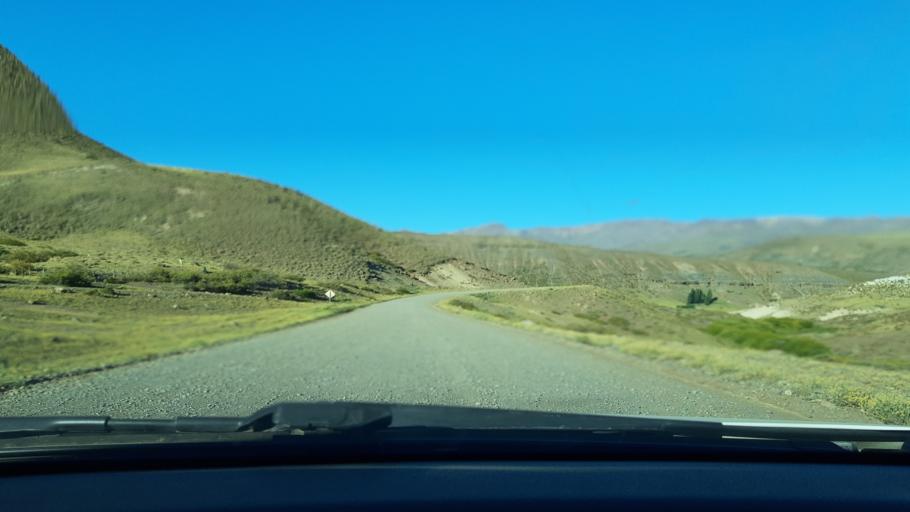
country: AR
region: Neuquen
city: Las Ovejas
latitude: -36.8222
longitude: -70.7054
